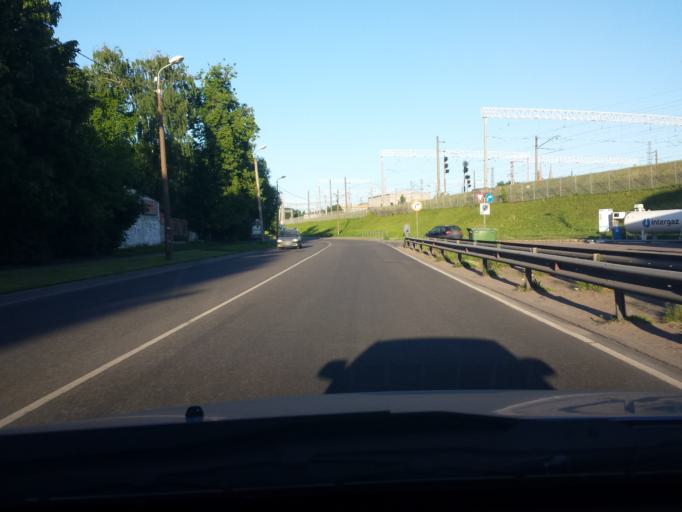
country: LV
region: Riga
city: Riga
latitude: 56.9474
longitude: 24.1286
